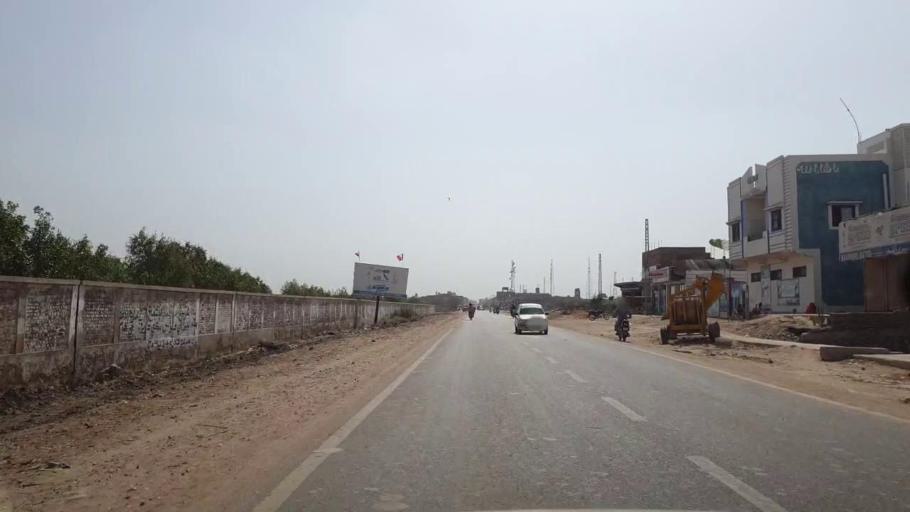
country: PK
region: Sindh
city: Matli
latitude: 25.0516
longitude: 68.6477
